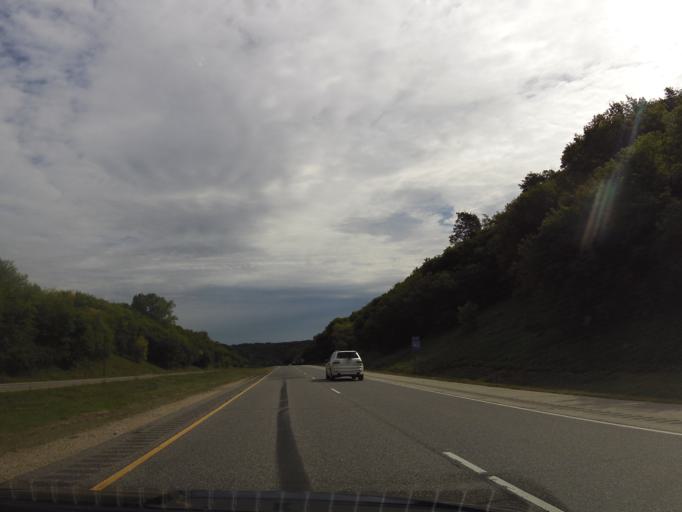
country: US
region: Wisconsin
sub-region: Trempealeau County
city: Trempealeau
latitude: 43.9298
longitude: -91.4321
